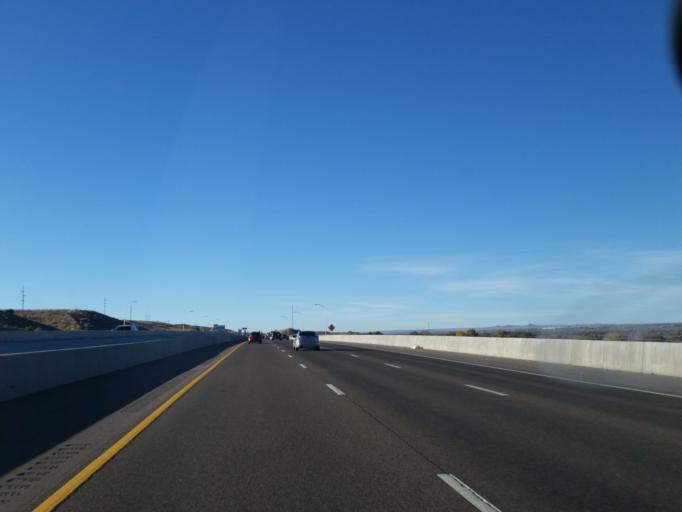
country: US
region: New Mexico
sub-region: Sandoval County
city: Bernalillo
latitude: 35.2954
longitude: -106.5431
